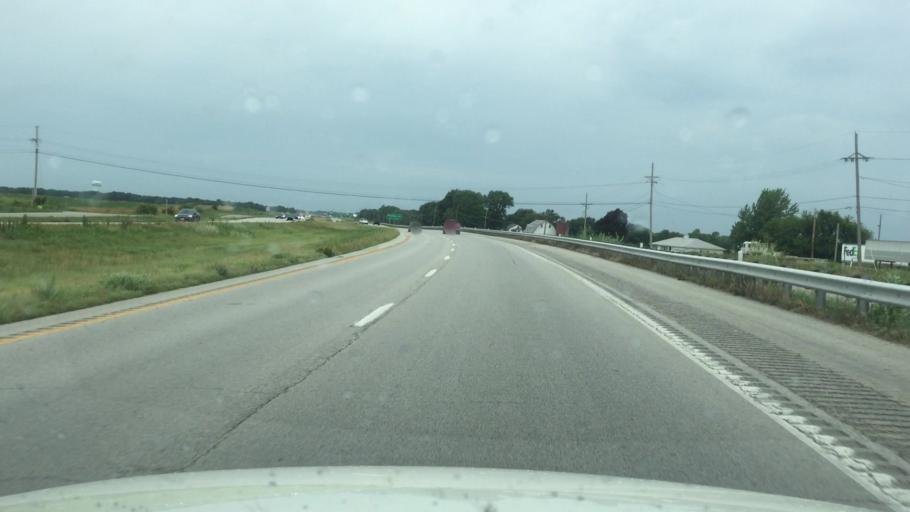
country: US
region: Missouri
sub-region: Jackson County
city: Lake Lotawana
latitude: 38.9010
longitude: -94.3010
